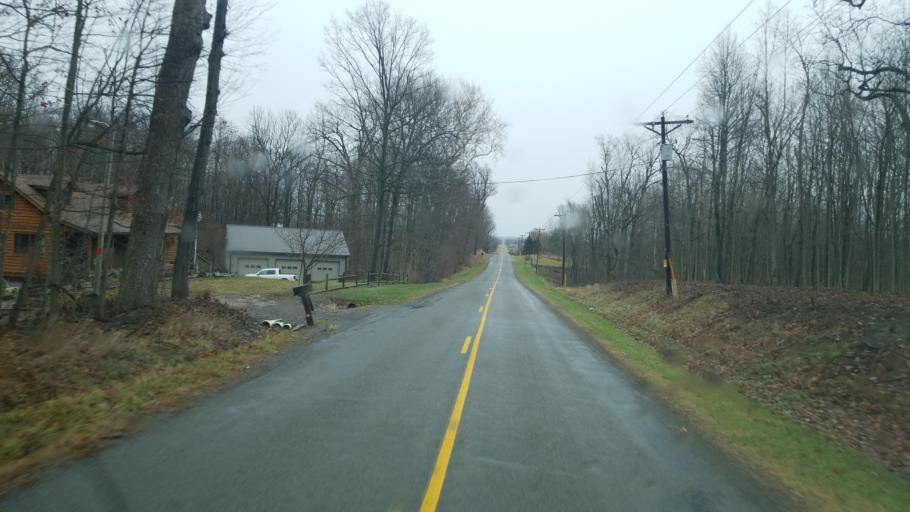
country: US
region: Ohio
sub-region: Logan County
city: Northwood
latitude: 40.4449
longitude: -83.6460
